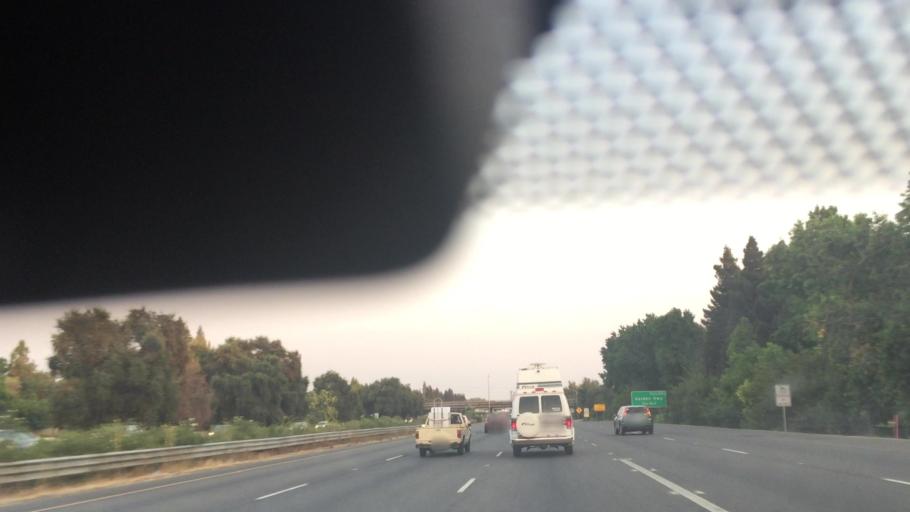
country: US
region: California
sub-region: Yolo County
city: West Sacramento
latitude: 38.6180
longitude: -121.5141
